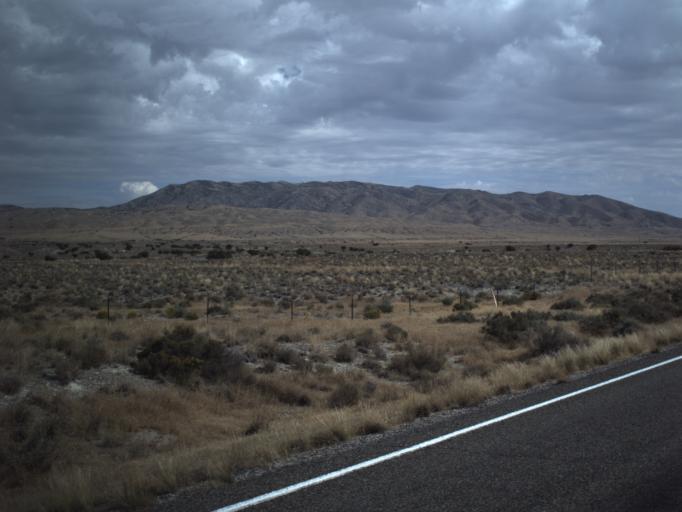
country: US
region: Utah
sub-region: Tooele County
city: Wendover
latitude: 41.4339
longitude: -113.7708
